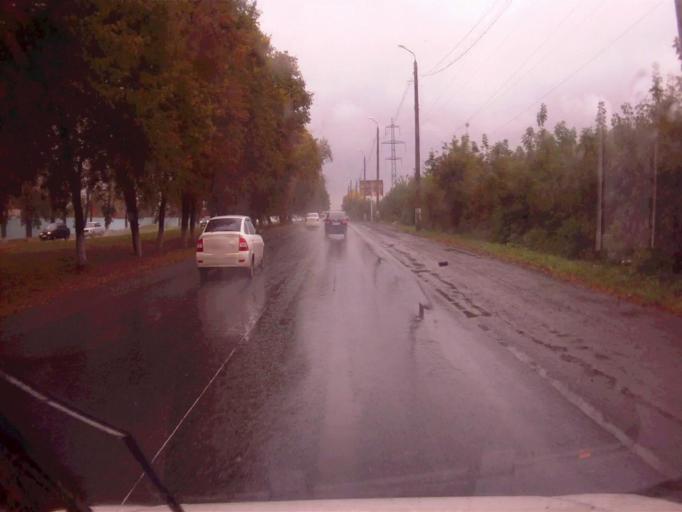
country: RU
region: Chelyabinsk
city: Dolgoderevenskoye
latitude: 55.2498
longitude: 61.3566
